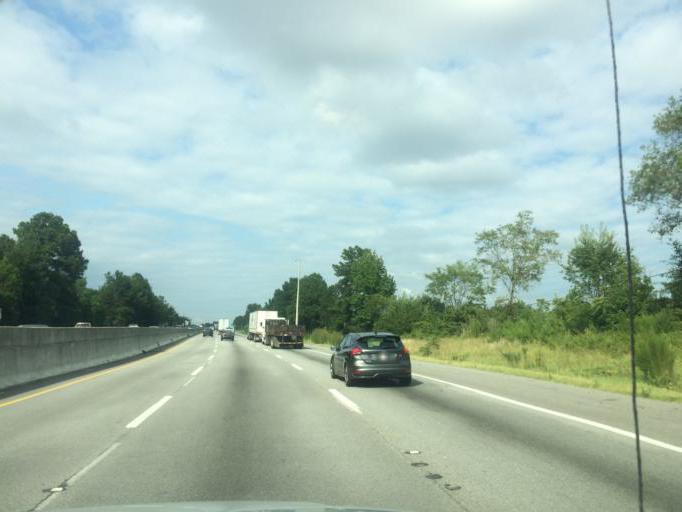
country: US
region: South Carolina
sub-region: Greenville County
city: Mauldin
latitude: 34.8054
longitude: -82.3489
